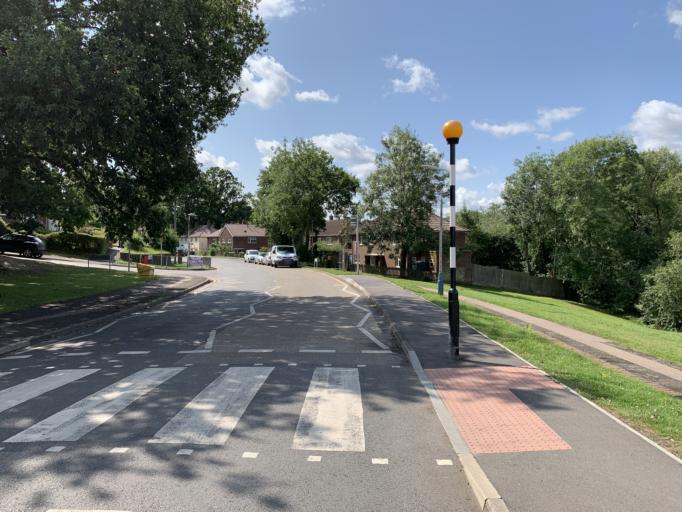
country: GB
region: England
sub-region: Kent
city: Tonbridge
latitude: 51.2149
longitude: 0.2922
